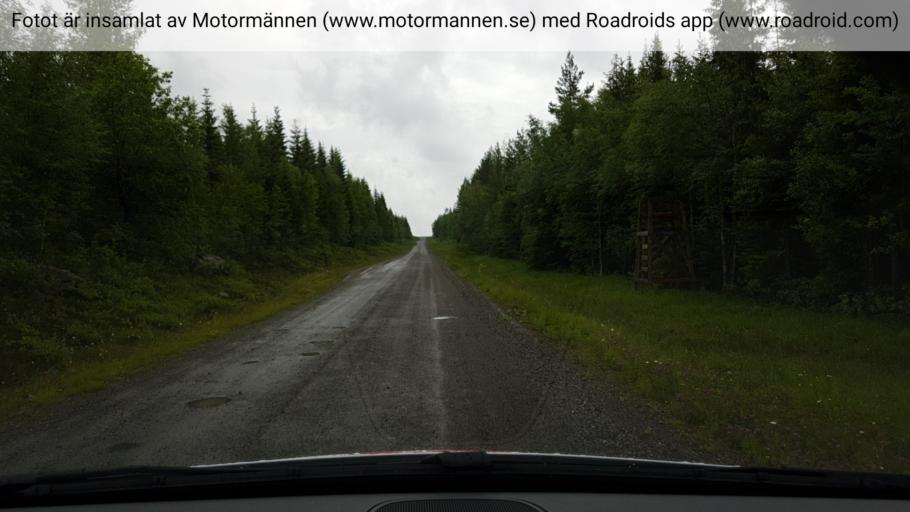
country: SE
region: Jaemtland
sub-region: Stroemsunds Kommun
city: Stroemsund
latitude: 64.2580
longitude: 15.0176
